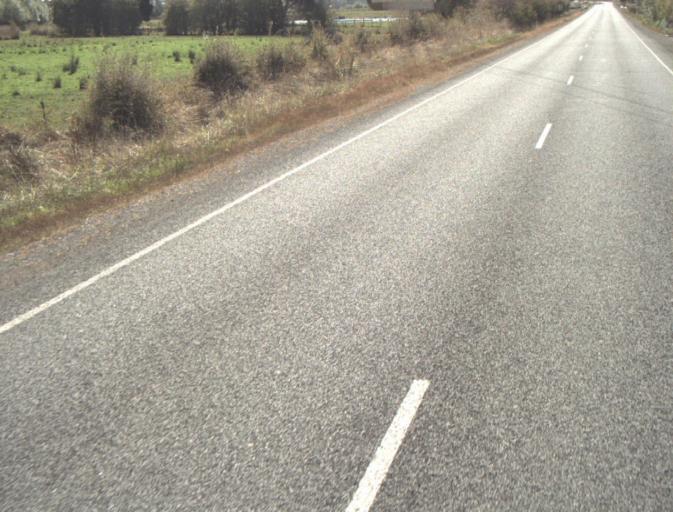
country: AU
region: Tasmania
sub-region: Launceston
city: Mayfield
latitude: -41.2444
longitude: 147.2170
